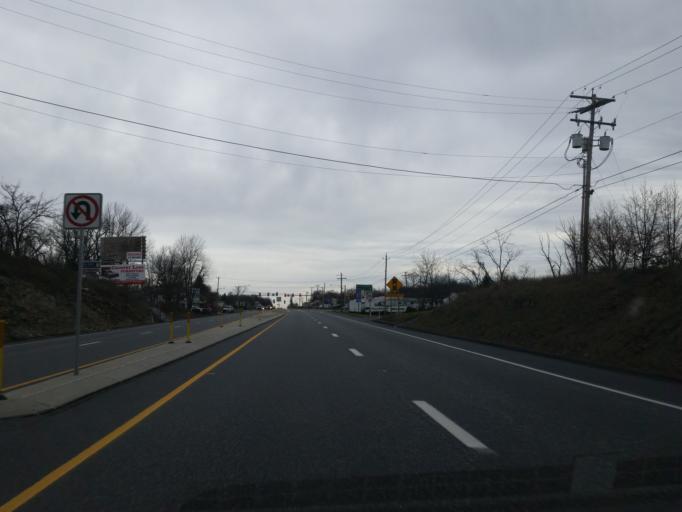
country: US
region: Pennsylvania
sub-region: Dauphin County
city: Skyline View
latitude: 40.3702
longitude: -76.6531
